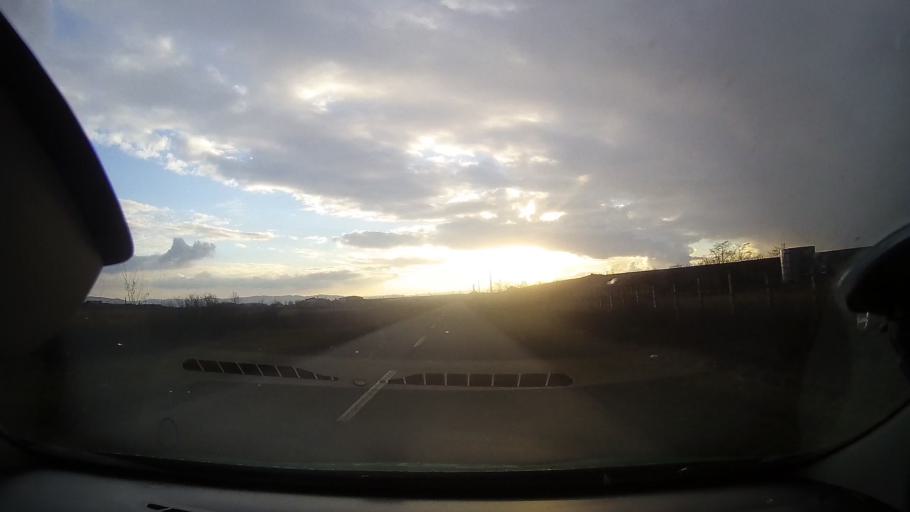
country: RO
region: Alba
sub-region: Comuna Lunca Muresului
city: Lunca Muresului
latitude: 46.4437
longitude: 23.9129
